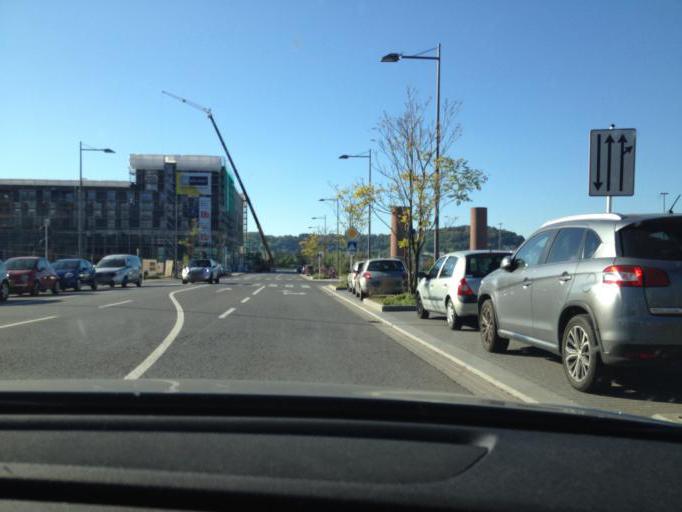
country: LU
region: Luxembourg
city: Belvaux
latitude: 49.5026
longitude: 5.9444
